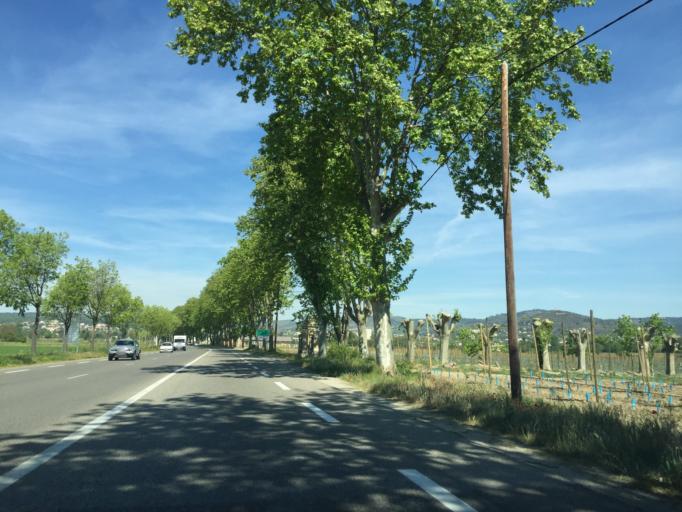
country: FR
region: Provence-Alpes-Cote d'Azur
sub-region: Departement des Alpes-de-Haute-Provence
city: Manosque
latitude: 43.8112
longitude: 5.8100
